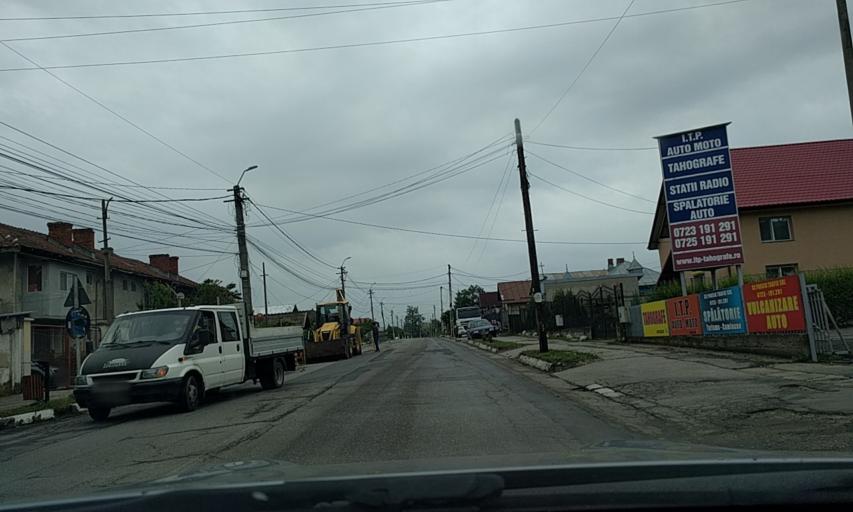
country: RO
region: Dambovita
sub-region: Oras Pucioasa
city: Glodeni
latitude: 45.0456
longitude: 25.4385
